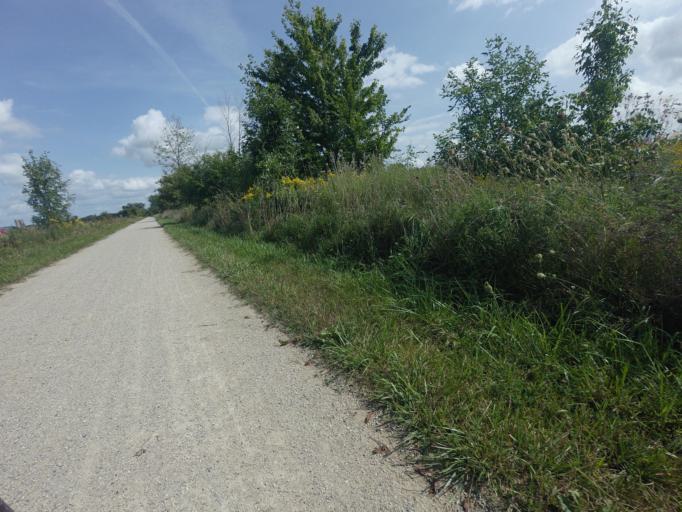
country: CA
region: Ontario
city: Waterloo
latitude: 43.5821
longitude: -80.7406
